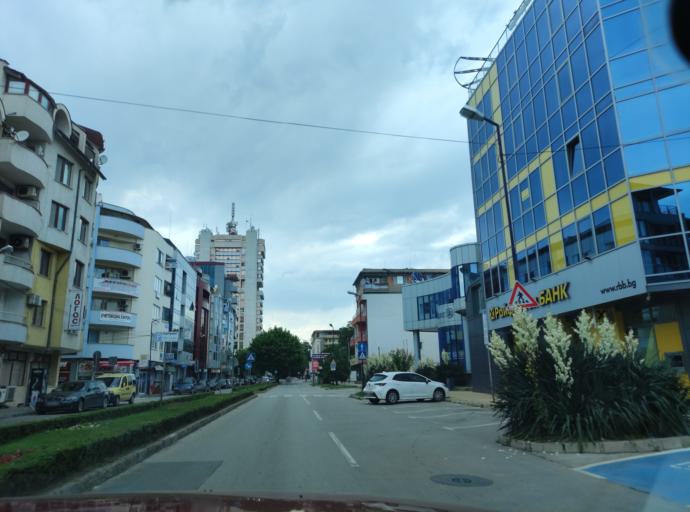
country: BG
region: Pazardzhik
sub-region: Obshtina Pazardzhik
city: Pazardzhik
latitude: 42.1875
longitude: 24.3338
